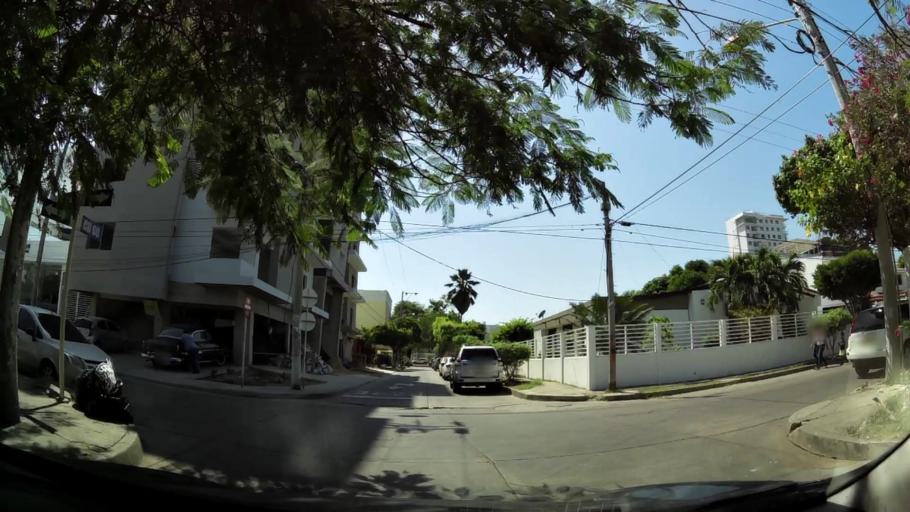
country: CO
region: Bolivar
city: Cartagena
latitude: 10.4456
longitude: -75.5182
